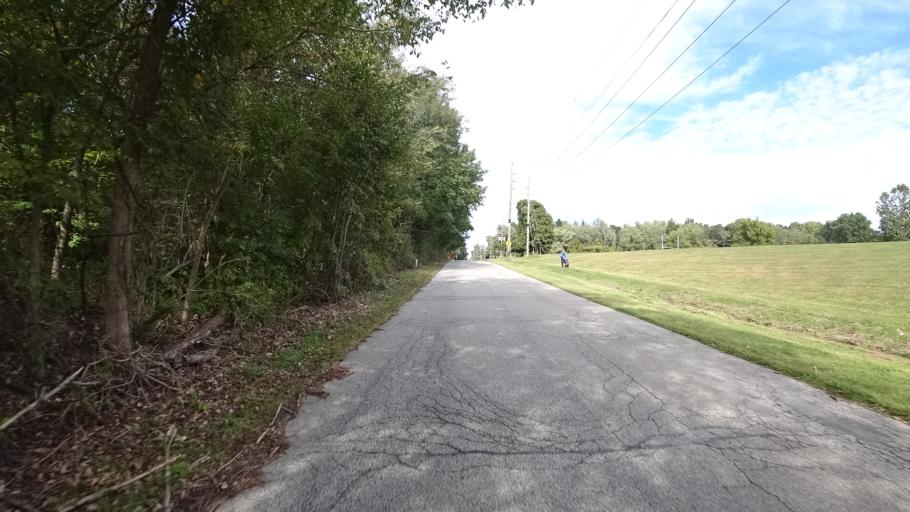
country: US
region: Indiana
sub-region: LaPorte County
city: Trail Creek
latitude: 41.7154
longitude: -86.8554
